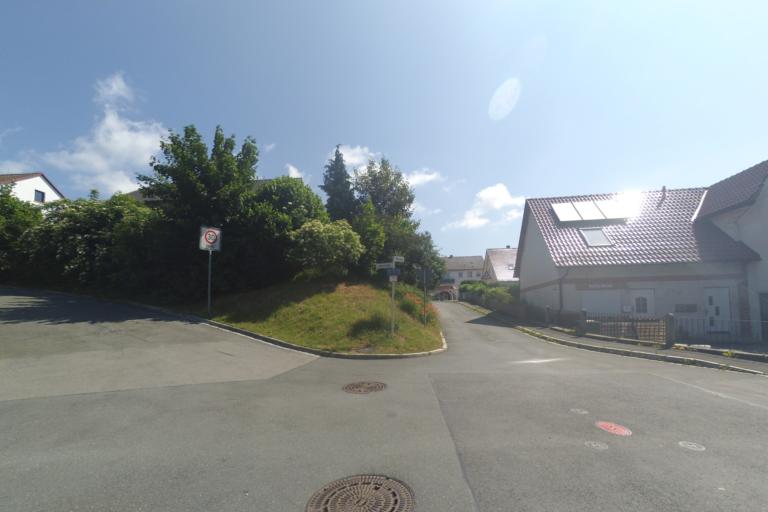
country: DE
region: Bavaria
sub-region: Upper Franconia
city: Burgkunstadt
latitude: 50.1365
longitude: 11.2547
